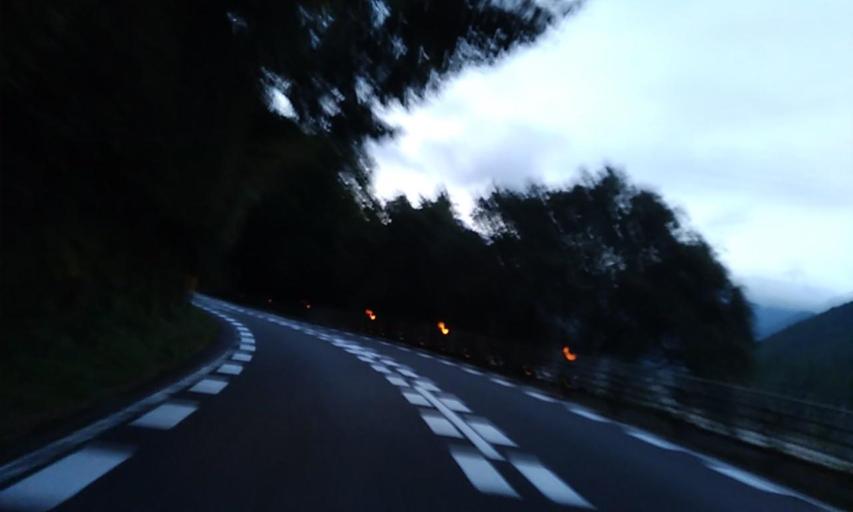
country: JP
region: Wakayama
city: Shingu
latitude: 33.7325
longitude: 135.9434
